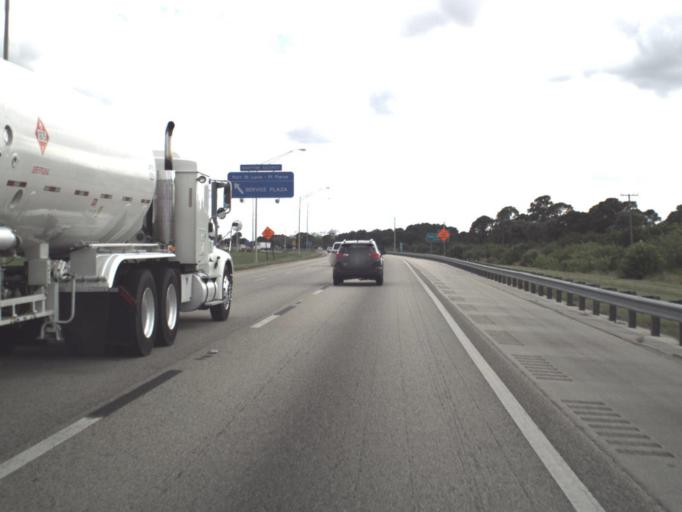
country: US
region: Florida
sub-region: Saint Lucie County
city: Port Saint Lucie
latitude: 27.3074
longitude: -80.3745
